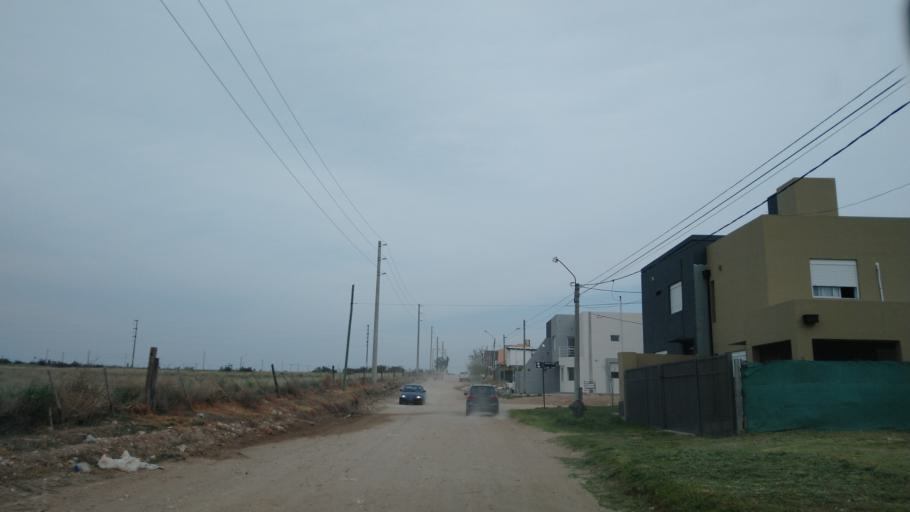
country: AR
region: Buenos Aires
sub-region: Partido de Bahia Blanca
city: Bahia Blanca
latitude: -38.6972
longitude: -62.2342
